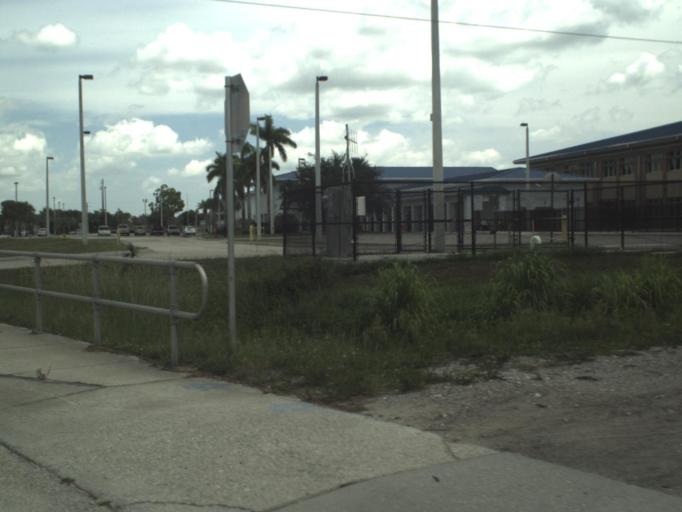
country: US
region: Florida
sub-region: Martin County
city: Palm City
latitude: 27.1683
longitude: -80.2509
